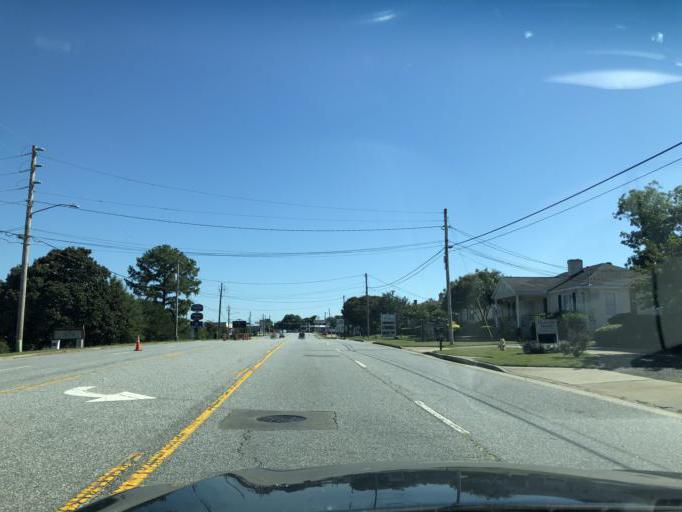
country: US
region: Georgia
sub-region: Muscogee County
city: Columbus
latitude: 32.5102
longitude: -84.9537
